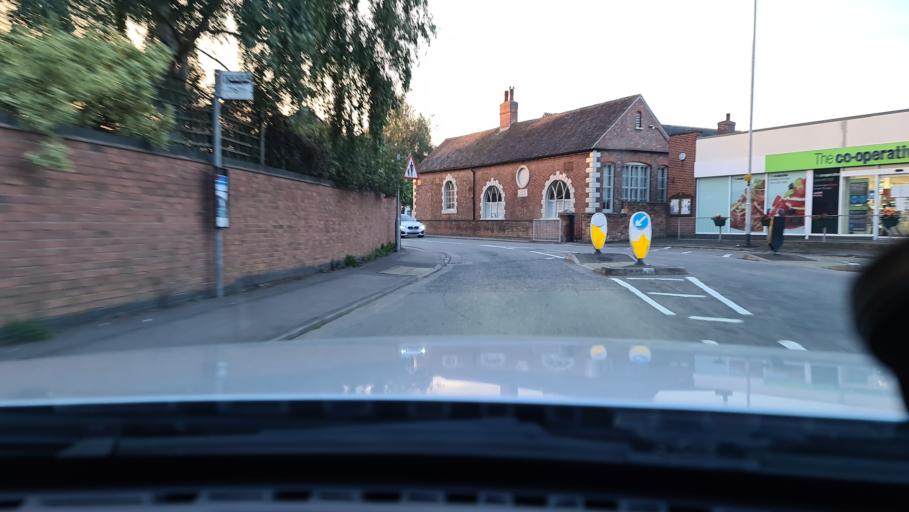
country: GB
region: England
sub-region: Leicestershire
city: Sapcote
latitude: 52.5366
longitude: -1.2807
